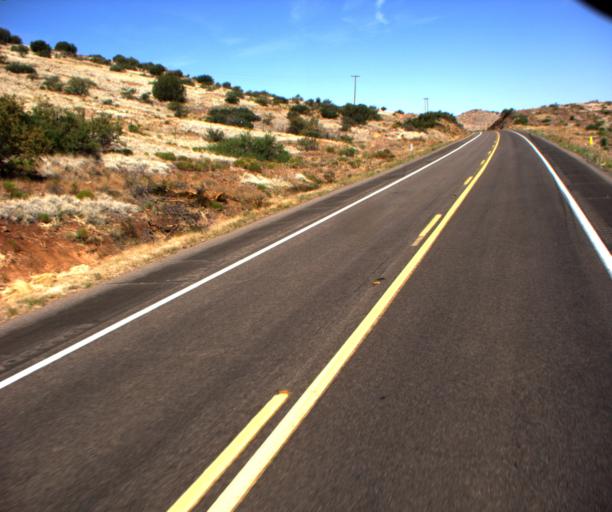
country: US
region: Arizona
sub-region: Greenlee County
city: Clifton
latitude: 32.7689
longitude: -109.2590
